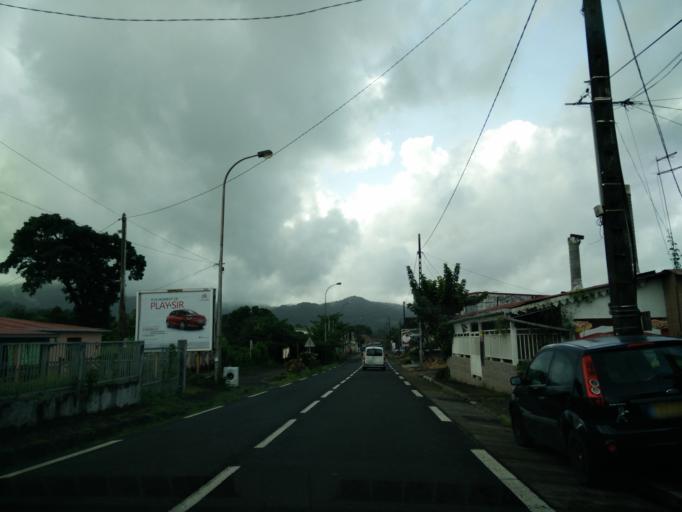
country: MQ
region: Martinique
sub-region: Martinique
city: Le Morne-Rouge
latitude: 14.7671
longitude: -61.1240
